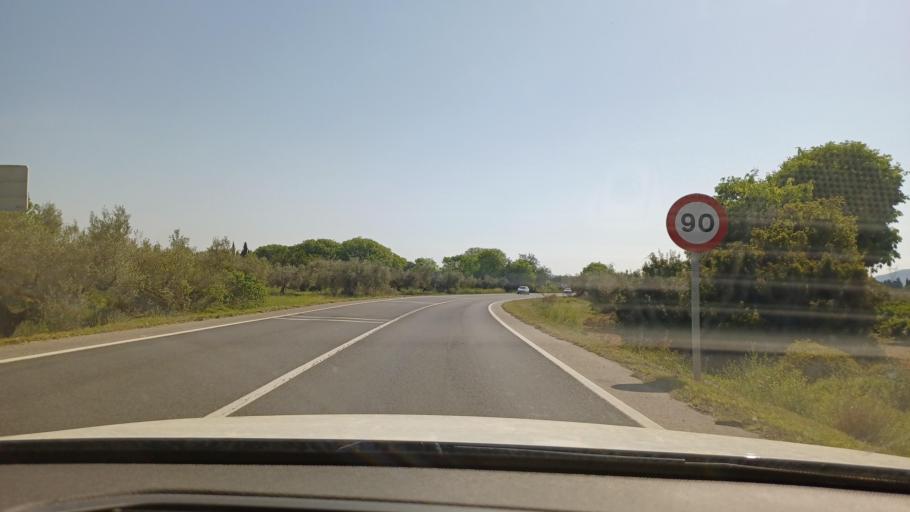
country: ES
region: Catalonia
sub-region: Provincia de Tarragona
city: Santa Barbara
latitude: 40.7059
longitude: 0.4840
